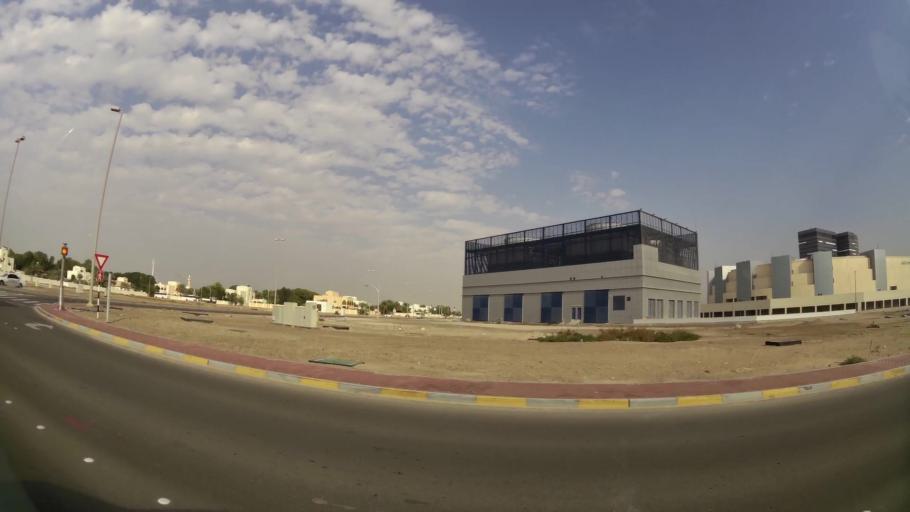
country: AE
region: Abu Dhabi
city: Abu Dhabi
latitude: 24.3781
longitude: 54.5274
